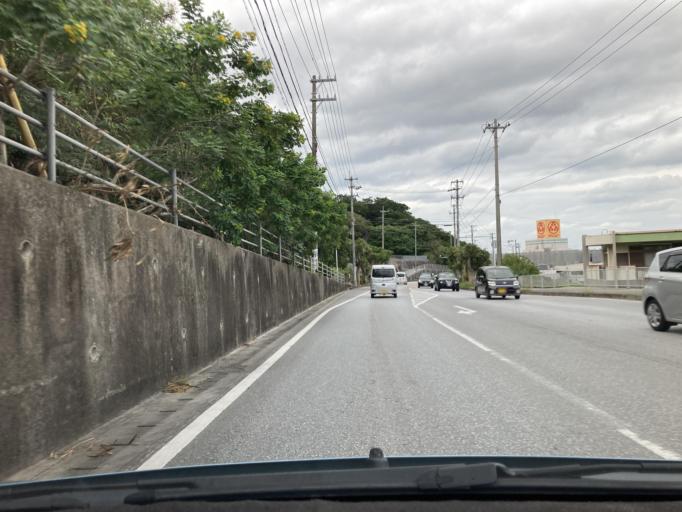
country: JP
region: Okinawa
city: Tomigusuku
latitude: 26.1738
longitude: 127.6886
